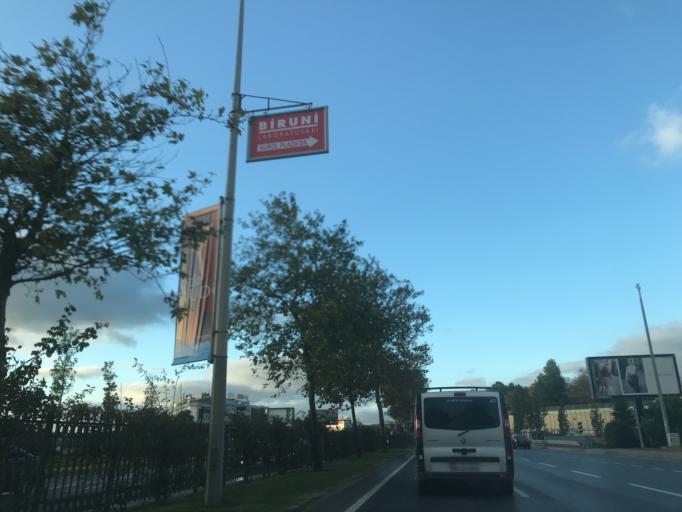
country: TR
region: Istanbul
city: Sisli
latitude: 41.1152
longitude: 29.0246
